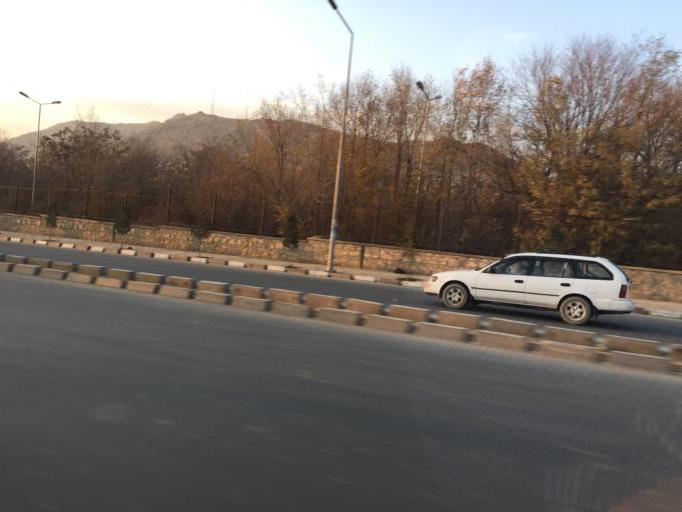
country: AF
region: Kabul
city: Kabul
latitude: 34.5334
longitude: 69.1243
